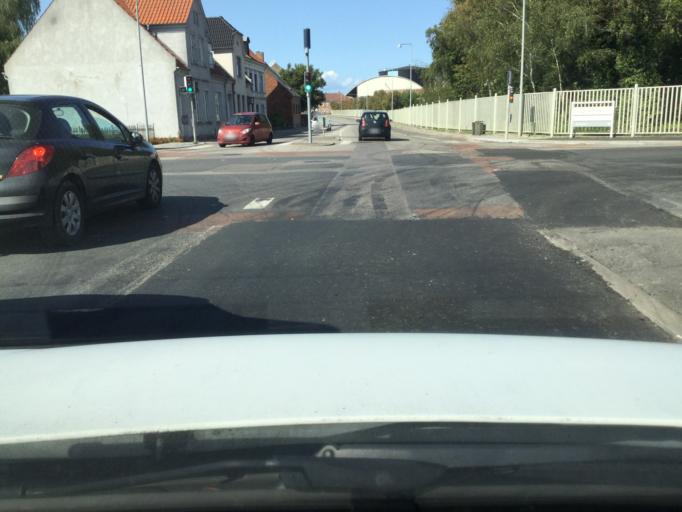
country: DK
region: Zealand
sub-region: Lolland Kommune
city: Nakskov
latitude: 54.8283
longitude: 11.1453
